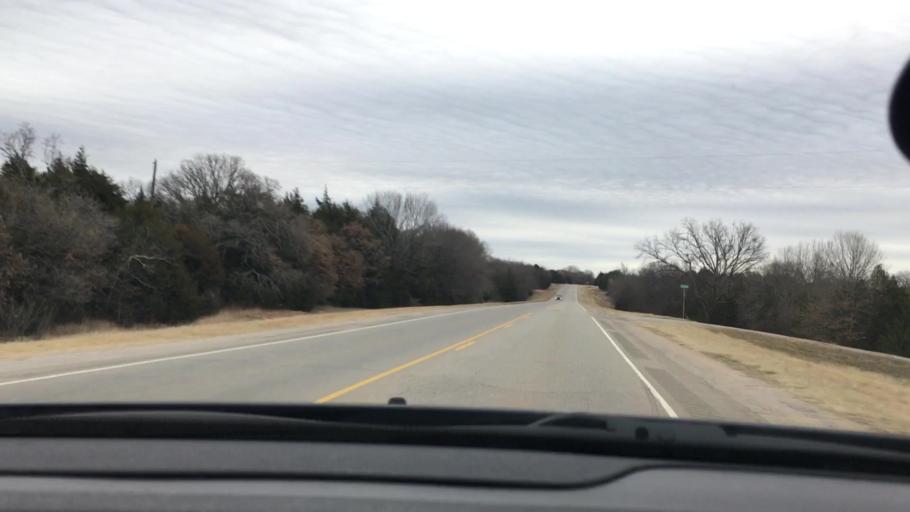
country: US
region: Oklahoma
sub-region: Johnston County
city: Tishomingo
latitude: 34.2381
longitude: -96.7744
